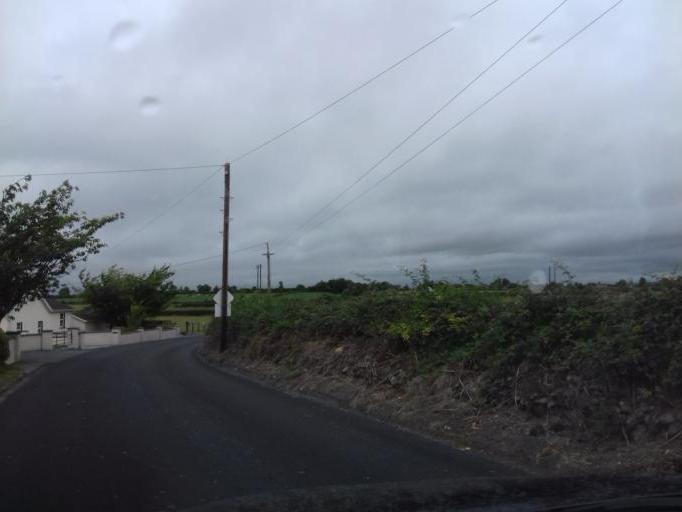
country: IE
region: Leinster
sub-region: Kilkenny
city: Graiguenamanagh
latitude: 52.6091
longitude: -7.0265
